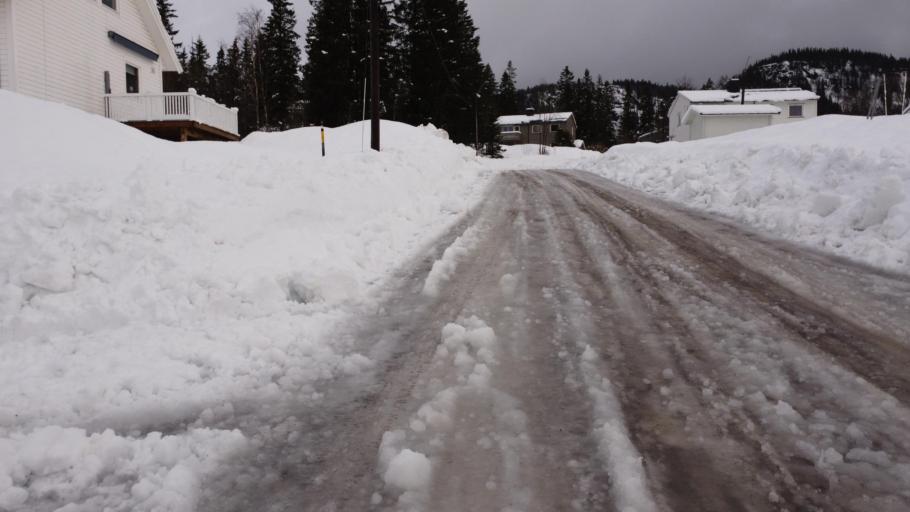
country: NO
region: Nordland
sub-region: Rana
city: Mo i Rana
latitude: 66.3347
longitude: 14.1453
